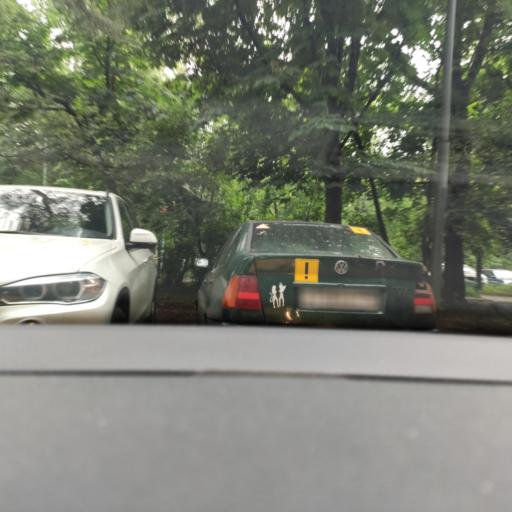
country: RU
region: Moscow
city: Metrogorodok
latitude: 55.8088
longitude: 37.7929
